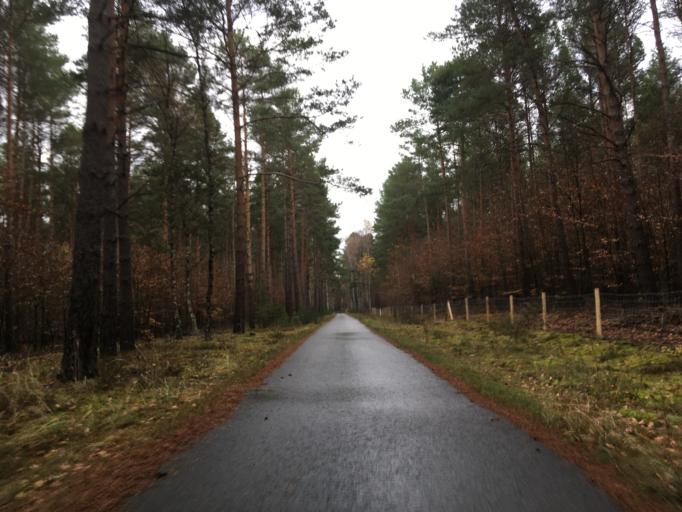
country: DE
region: Brandenburg
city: Jamlitz
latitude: 52.0524
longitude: 14.4801
